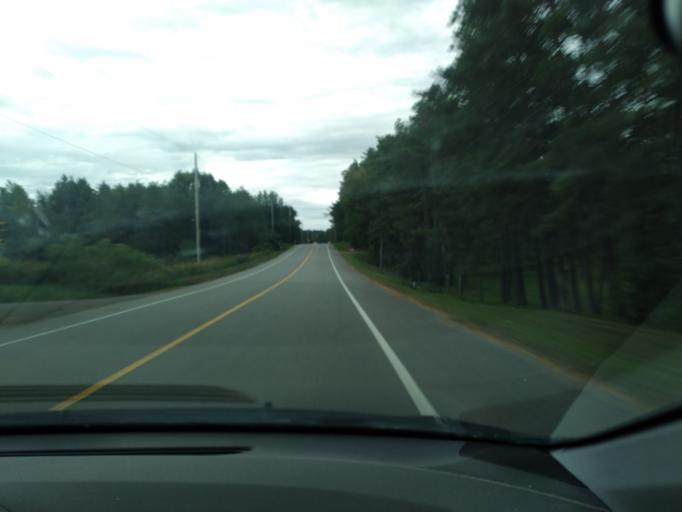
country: CA
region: Ontario
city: Bradford West Gwillimbury
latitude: 43.9764
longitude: -79.7999
